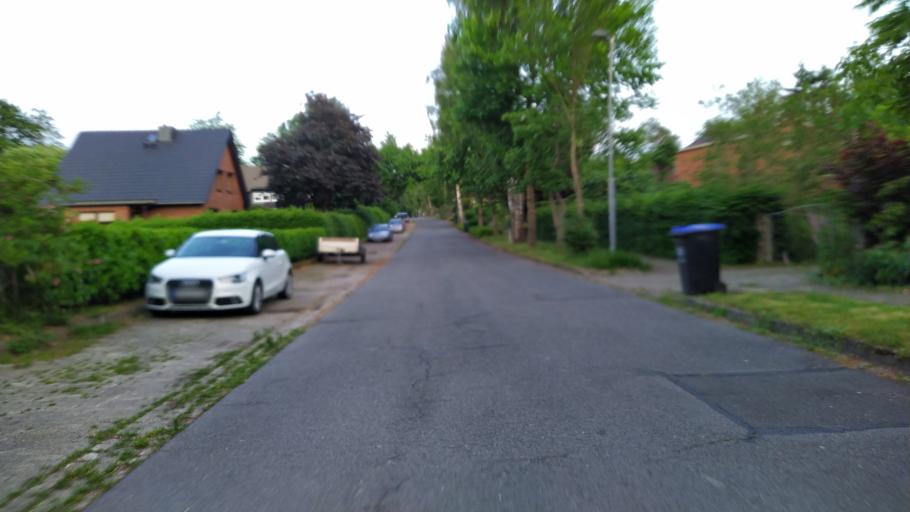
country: DE
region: Lower Saxony
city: Harsefeld
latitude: 53.4823
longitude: 9.5149
